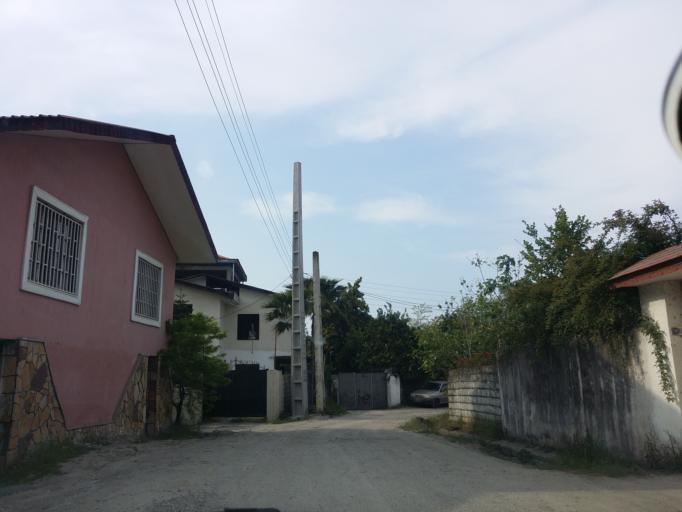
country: IR
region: Mazandaran
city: Chalus
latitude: 36.6799
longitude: 51.3929
